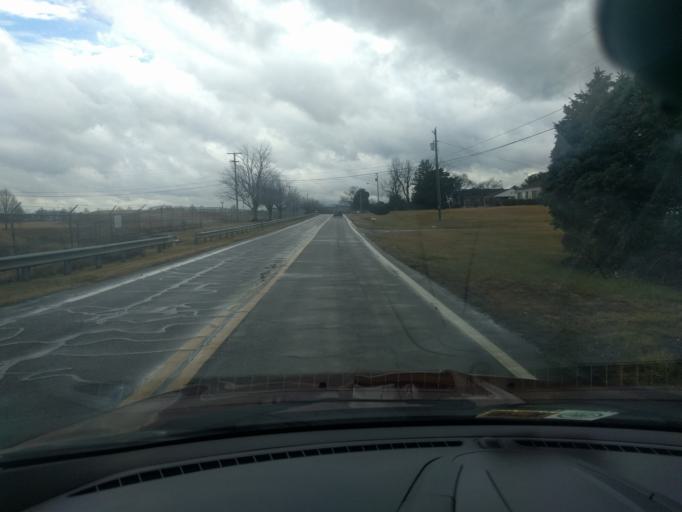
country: US
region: Virginia
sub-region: Roanoke County
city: Hollins
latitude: 37.3186
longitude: -79.9804
